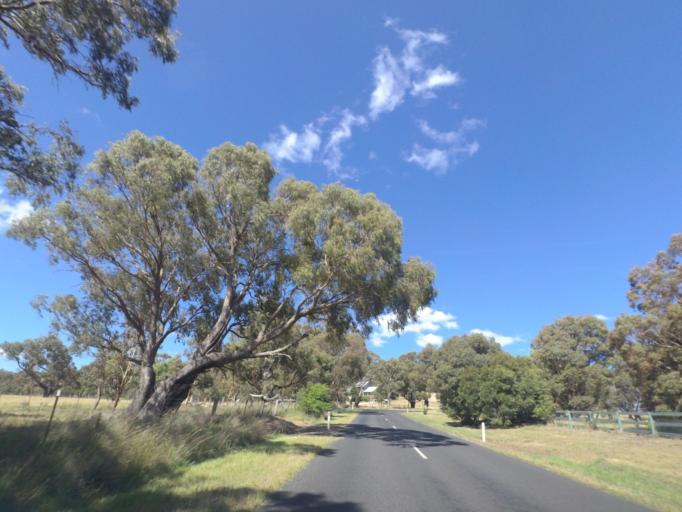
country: AU
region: Victoria
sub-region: Hume
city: Sunbury
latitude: -37.4288
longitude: 144.6150
